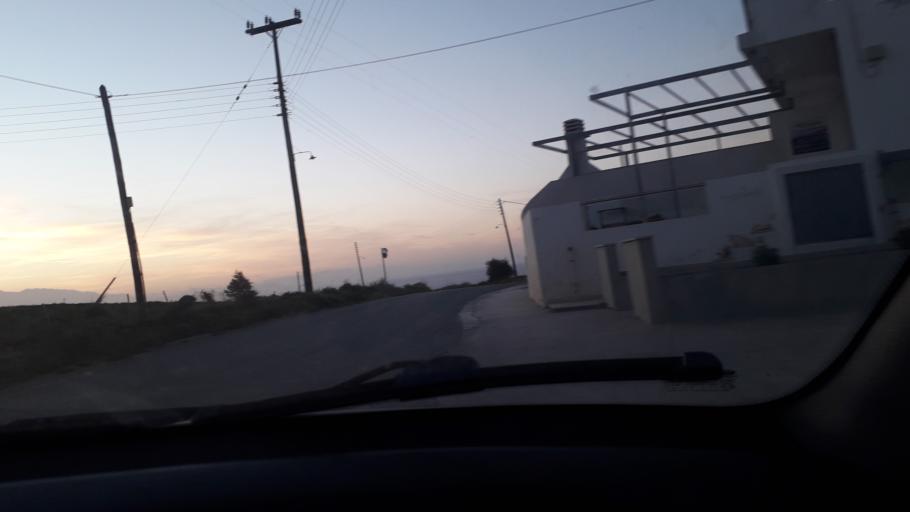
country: GR
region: Crete
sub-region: Nomos Rethymnis
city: Panormos
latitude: 35.3876
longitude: 24.6131
